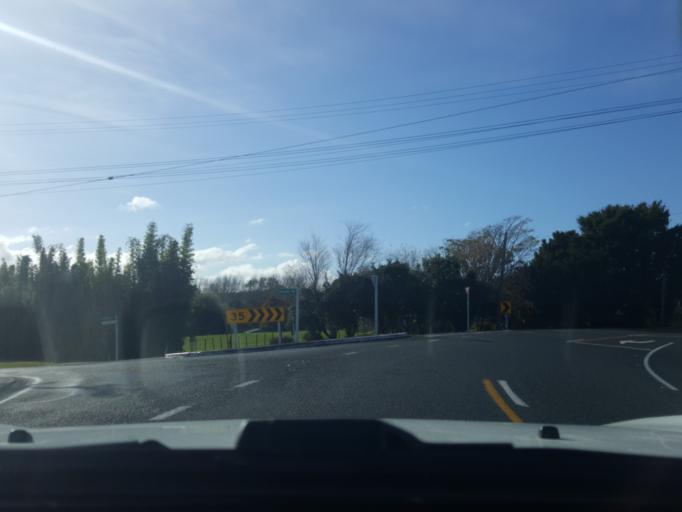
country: NZ
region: Auckland
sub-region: Auckland
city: Muriwai Beach
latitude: -36.7744
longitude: 174.5641
